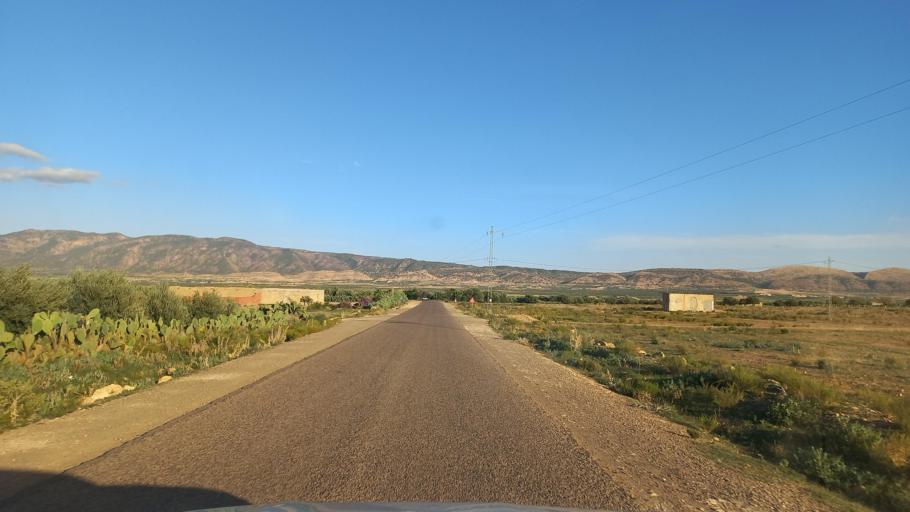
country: TN
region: Al Qasrayn
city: Sbiba
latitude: 35.4119
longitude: 9.1305
